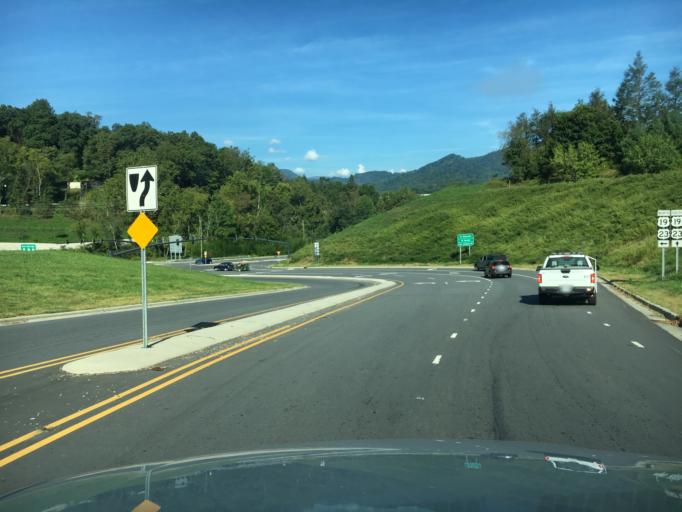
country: US
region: North Carolina
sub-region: Haywood County
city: Lake Junaluska
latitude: 35.5246
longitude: -82.9566
